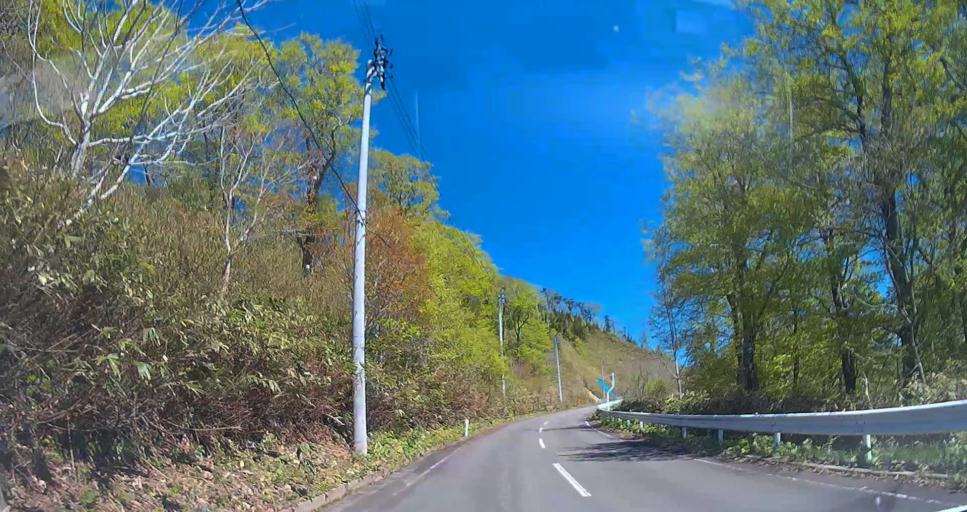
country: JP
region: Aomori
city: Aomori Shi
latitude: 41.2239
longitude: 140.8039
